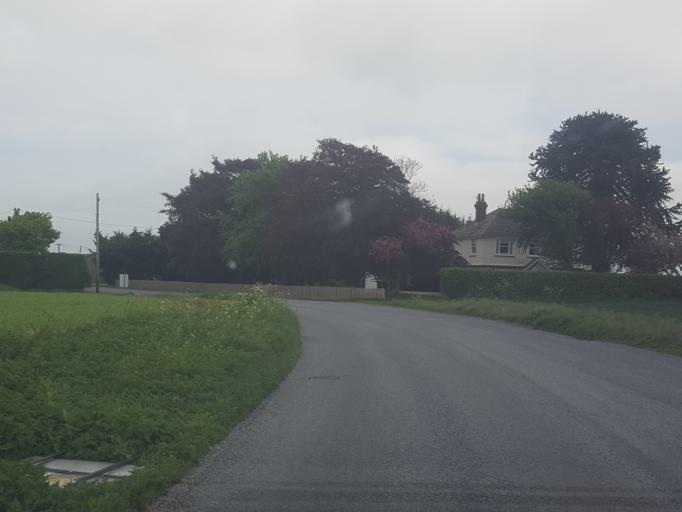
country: GB
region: England
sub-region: Essex
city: Frinton-on-Sea
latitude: 51.8527
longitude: 1.1982
